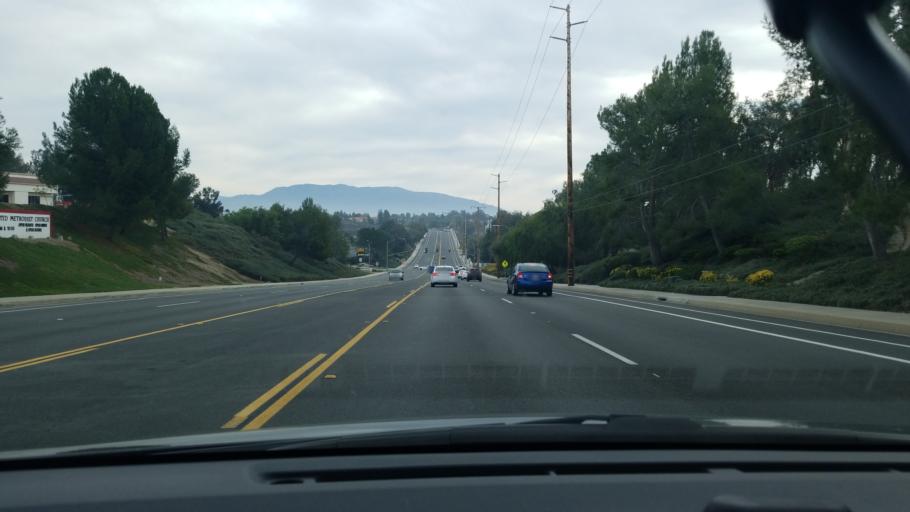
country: US
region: California
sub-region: Riverside County
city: Temecula
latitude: 33.5034
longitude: -117.1221
